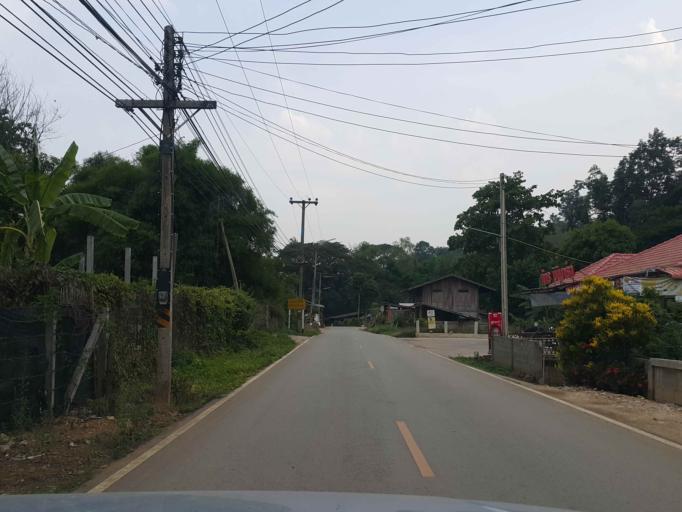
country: TH
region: Chiang Mai
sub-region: Amphoe Chiang Dao
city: Chiang Dao
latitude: 19.3901
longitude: 98.9299
